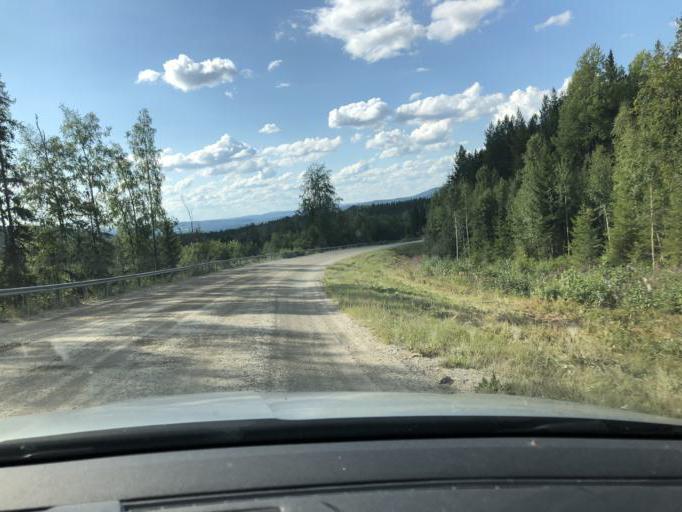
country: SE
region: Vaesternorrland
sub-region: Solleftea Kommun
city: Solleftea
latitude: 63.3142
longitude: 17.2221
